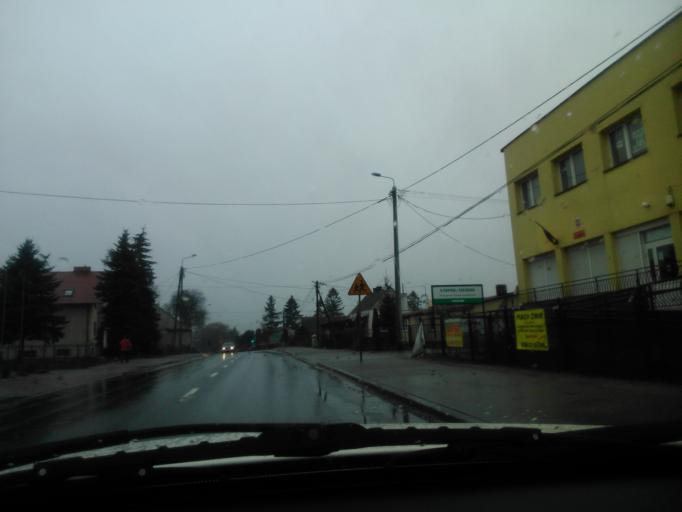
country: PL
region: Kujawsko-Pomorskie
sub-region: Powiat golubsko-dobrzynski
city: Radomin
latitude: 53.0865
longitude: 19.1958
